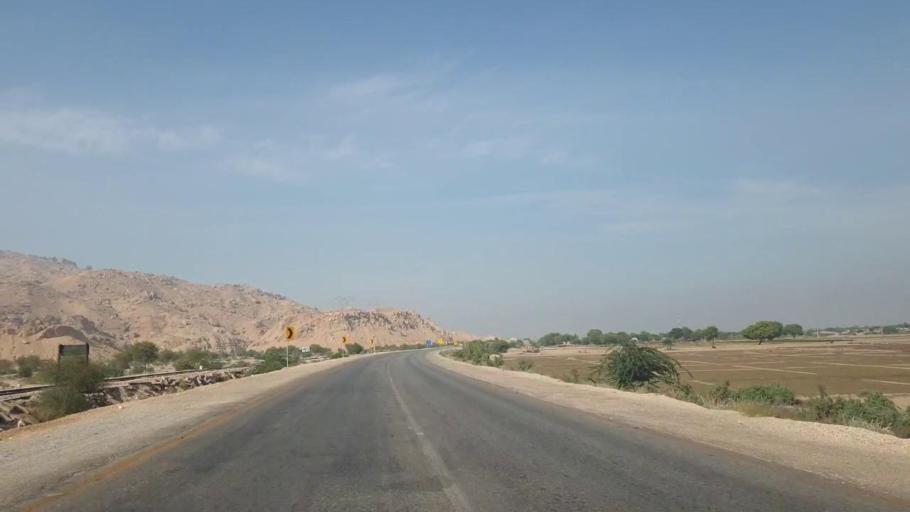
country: PK
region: Sindh
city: Sehwan
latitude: 26.2854
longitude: 67.8949
